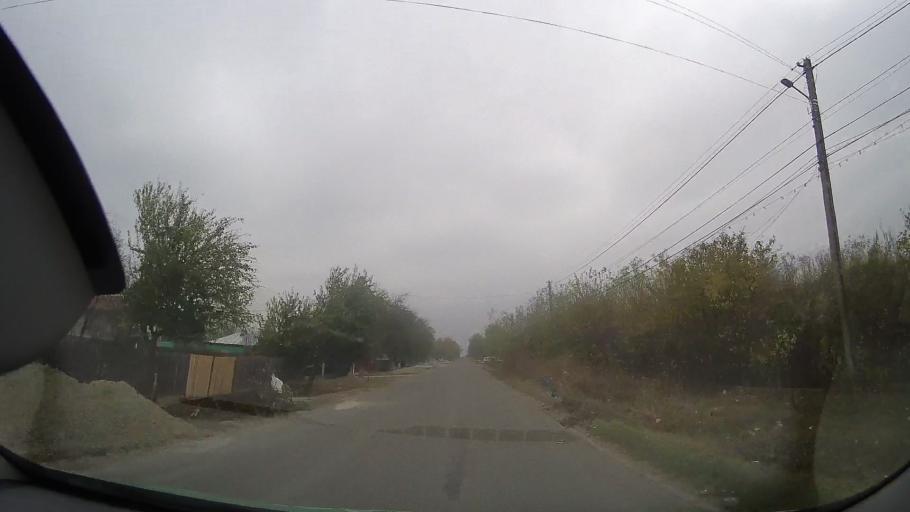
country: RO
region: Buzau
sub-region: Comuna Glodeanu-Silistea
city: Glodeanu-Silistea
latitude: 44.8200
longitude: 26.8360
